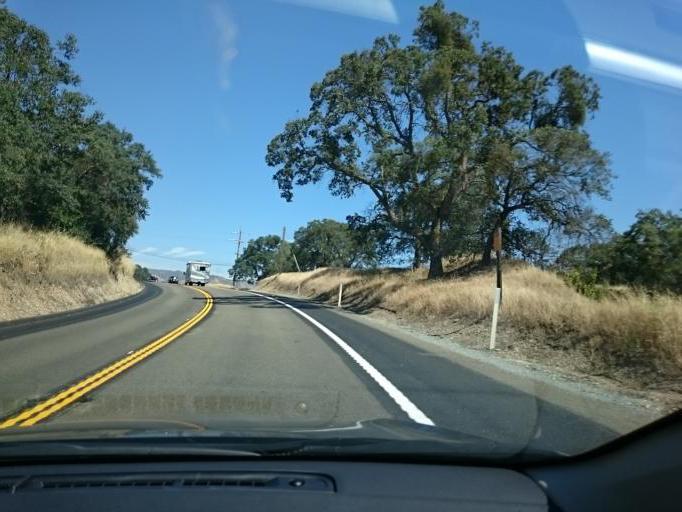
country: US
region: California
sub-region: Calaveras County
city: Valley Springs
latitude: 38.1848
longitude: -120.8432
